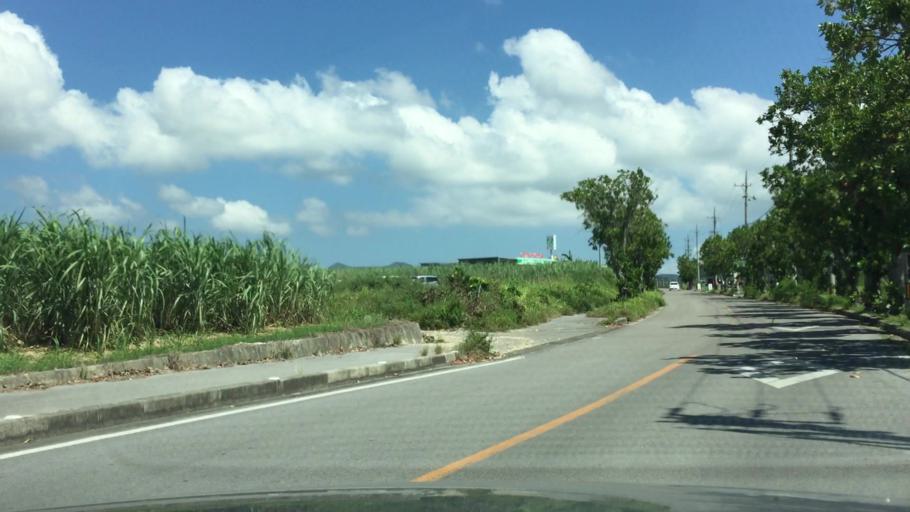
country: JP
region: Okinawa
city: Ishigaki
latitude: 24.3871
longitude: 124.2440
